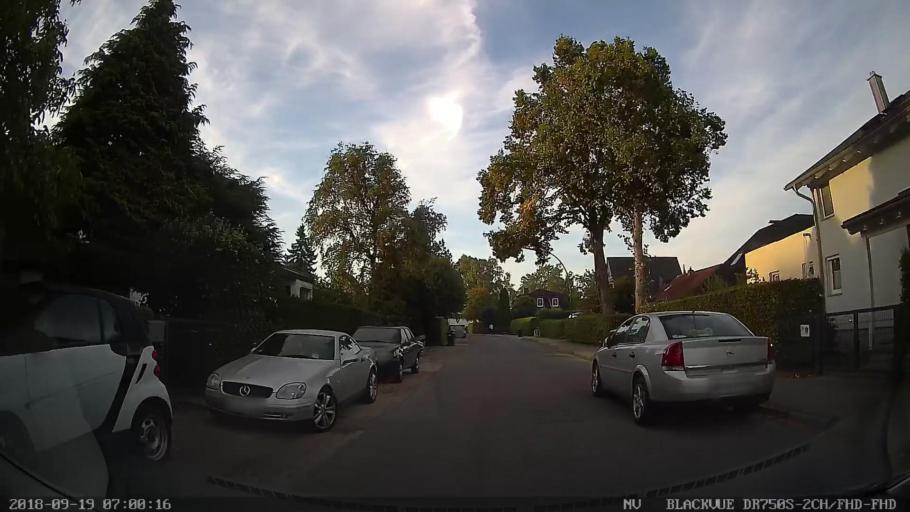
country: DE
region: Hamburg
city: Eidelstedt
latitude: 53.6319
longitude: 9.8950
